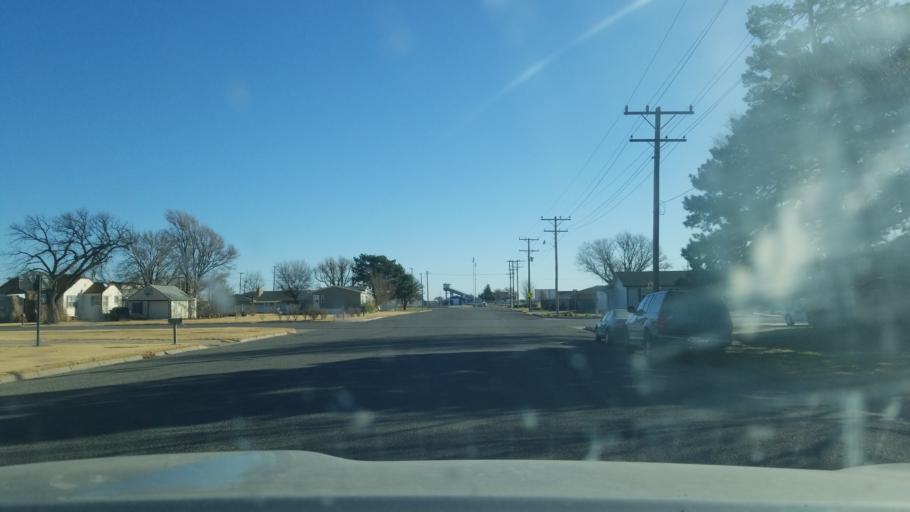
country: US
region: Kansas
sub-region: Ness County
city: Ness City
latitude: 38.4538
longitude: -99.9002
